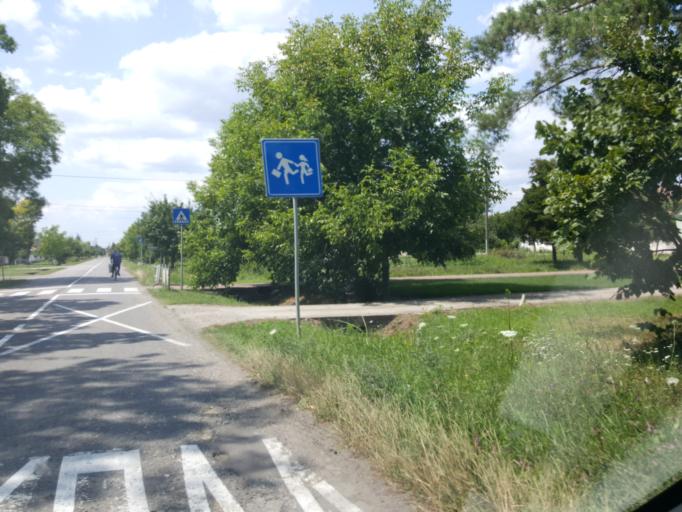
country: RS
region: Autonomna Pokrajina Vojvodina
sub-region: Sremski Okrug
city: Pecinci
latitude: 44.8447
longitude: 19.9582
